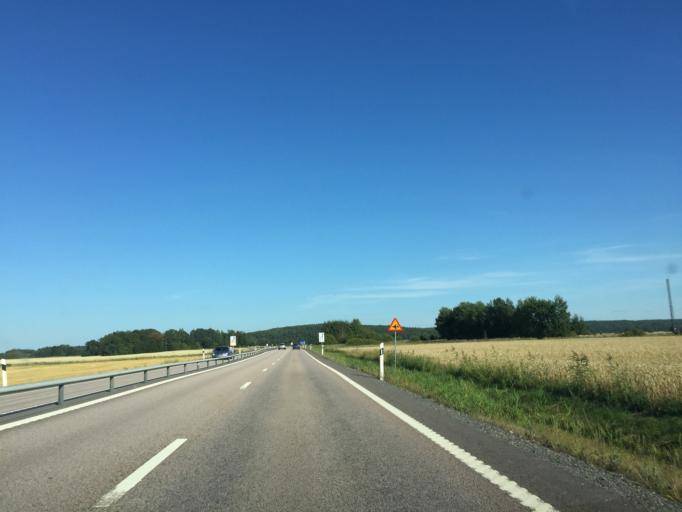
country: SE
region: Vaestmanland
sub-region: Arboga Kommun
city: Arboga
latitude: 59.3973
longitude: 15.9036
